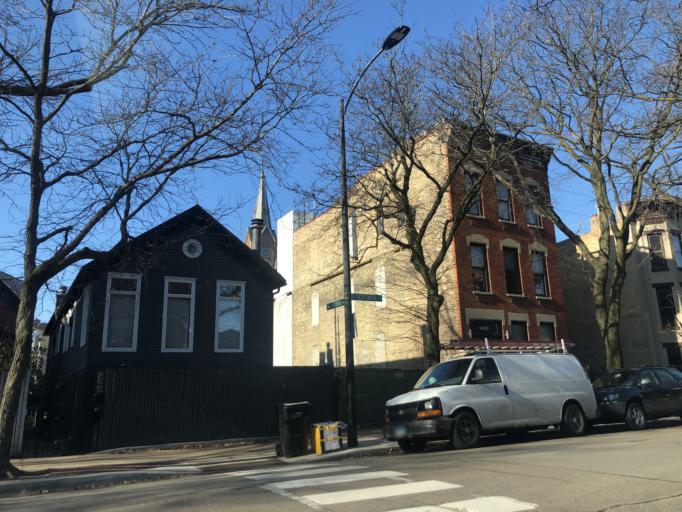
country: US
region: Illinois
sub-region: Cook County
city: Chicago
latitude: 41.9120
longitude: -87.6386
